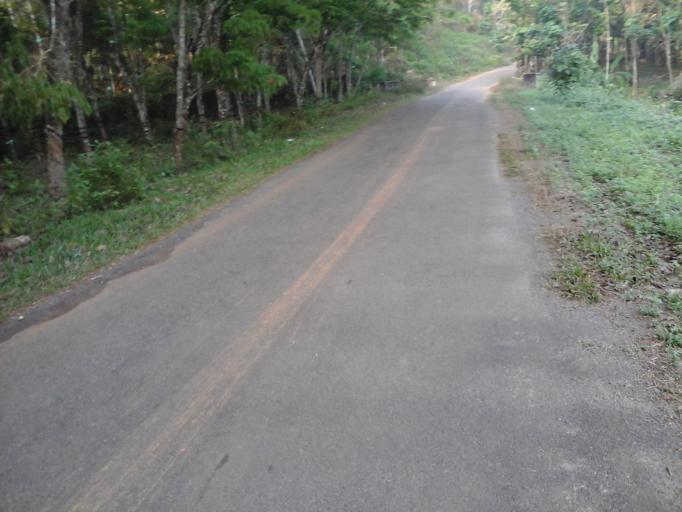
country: IN
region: Kerala
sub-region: Kottayam
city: Lalam
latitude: 9.5929
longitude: 76.7184
